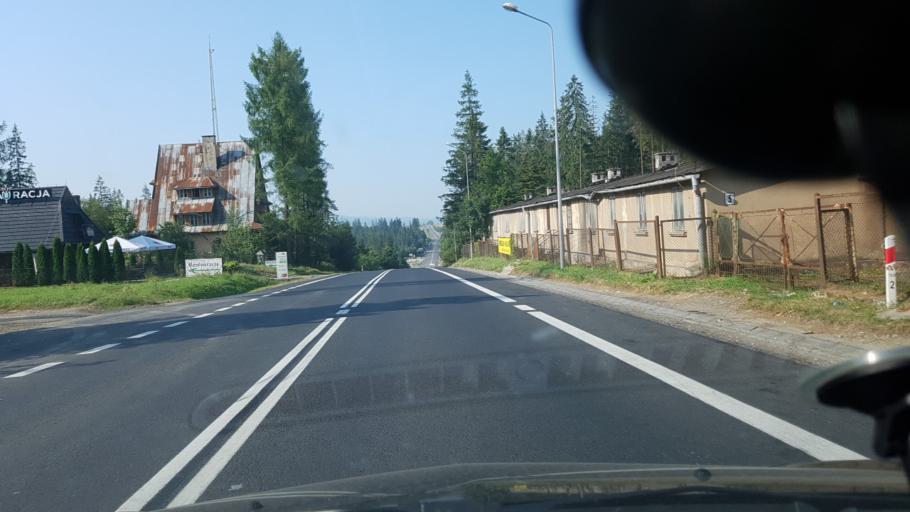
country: PL
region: Lesser Poland Voivodeship
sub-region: Powiat nowotarski
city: Chyzne
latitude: 49.4116
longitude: 19.6622
